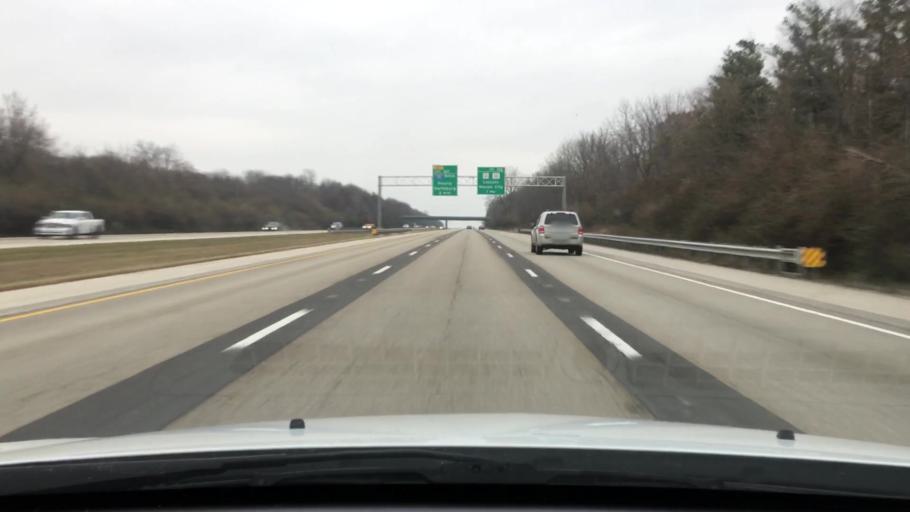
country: US
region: Illinois
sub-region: Logan County
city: Lincoln
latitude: 40.1419
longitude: -89.4170
